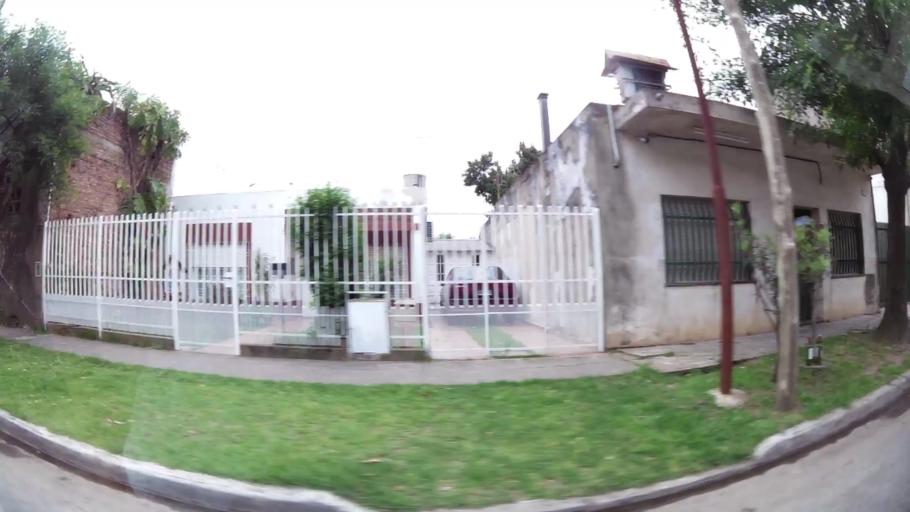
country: AR
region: Buenos Aires
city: San Justo
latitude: -34.7058
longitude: -58.5715
